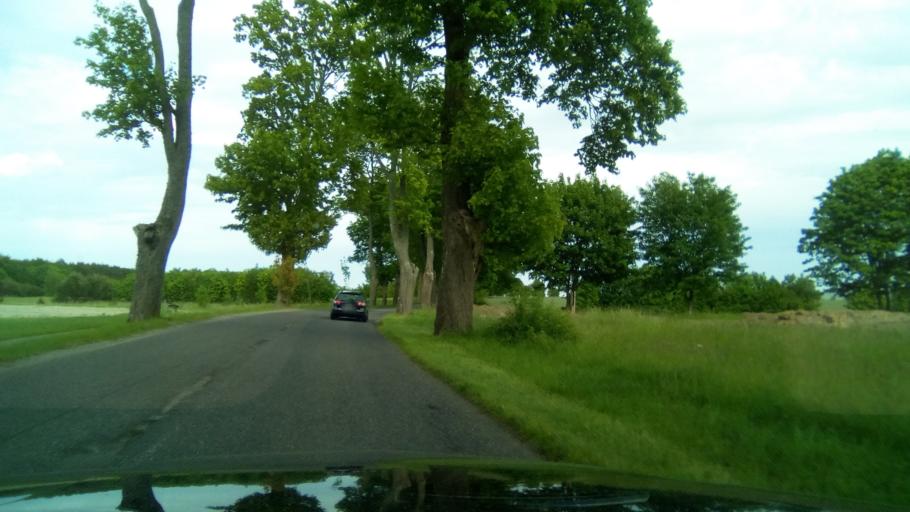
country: PL
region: Pomeranian Voivodeship
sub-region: Powiat pucki
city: Wierzchucino
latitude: 54.7904
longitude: 17.9814
